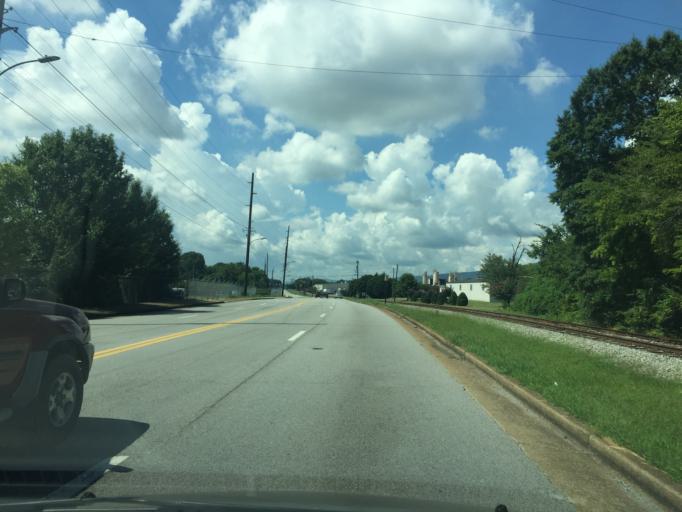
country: US
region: Tennessee
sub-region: Hamilton County
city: East Chattanooga
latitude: 35.0514
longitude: -85.2757
